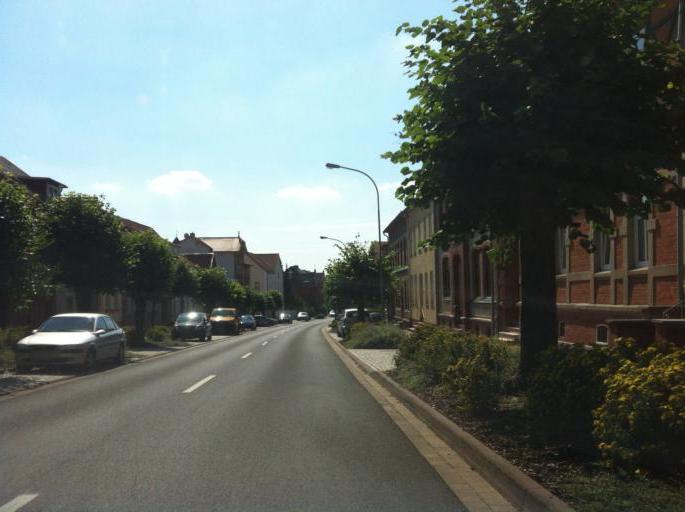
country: DE
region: Thuringia
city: Dingelstadt
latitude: 51.3181
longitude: 10.3162
